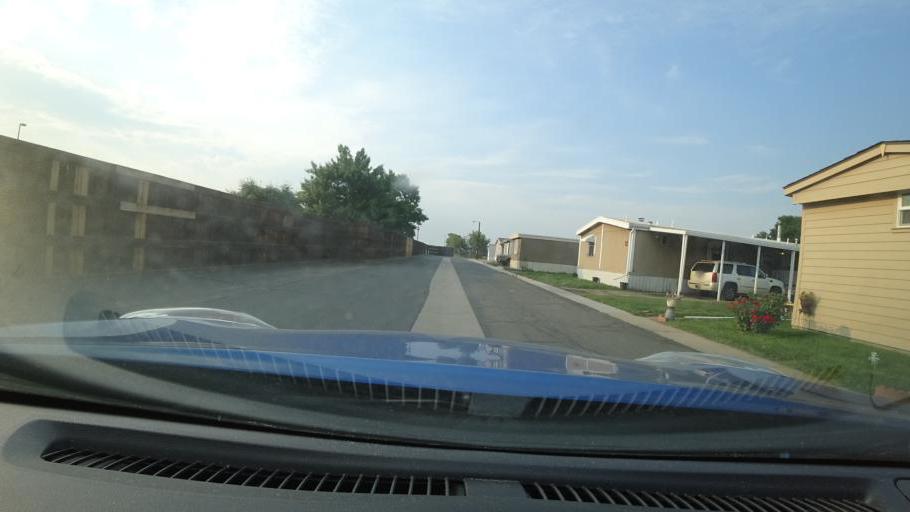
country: US
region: Colorado
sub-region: Adams County
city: Aurora
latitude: 39.7465
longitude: -104.7910
